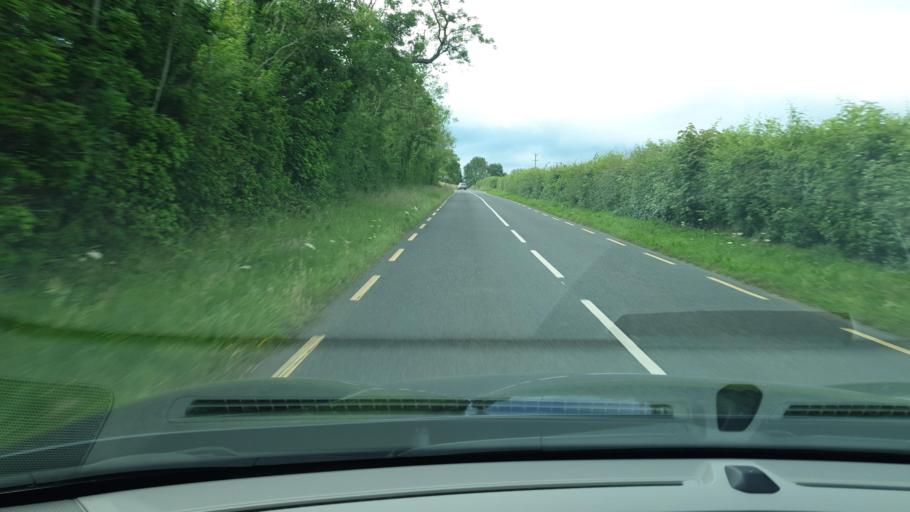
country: IE
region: Leinster
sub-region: An Mhi
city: Dunshaughlin
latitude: 53.5406
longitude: -6.5053
